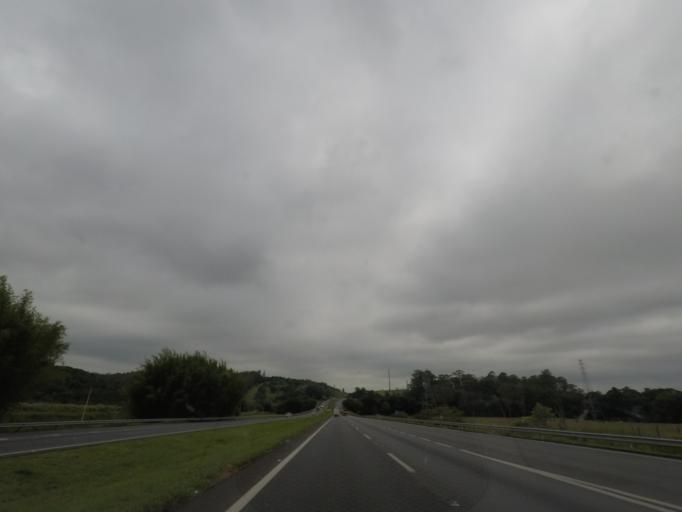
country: BR
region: Sao Paulo
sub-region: Itatiba
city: Itatiba
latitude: -22.9581
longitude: -46.8531
